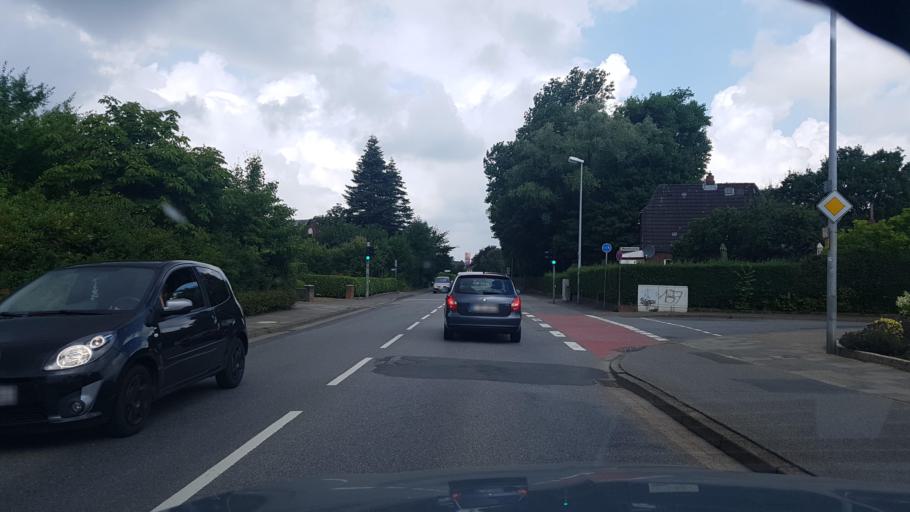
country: DE
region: Schleswig-Holstein
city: Husum
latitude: 54.4886
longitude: 9.0403
